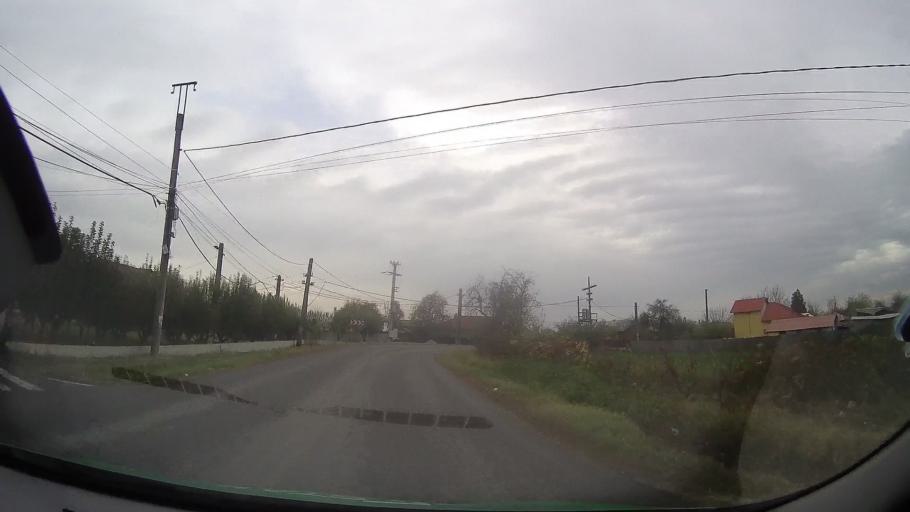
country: RO
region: Prahova
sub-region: Comuna Valea Calugareasca
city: Pantazi
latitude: 44.9125
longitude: 26.1588
